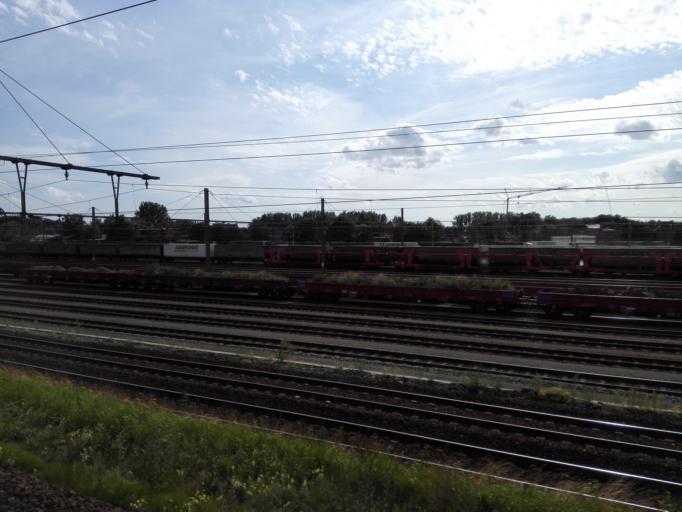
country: BE
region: Flanders
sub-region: Provincie Antwerpen
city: Mechelen
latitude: 51.0128
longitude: 4.5084
